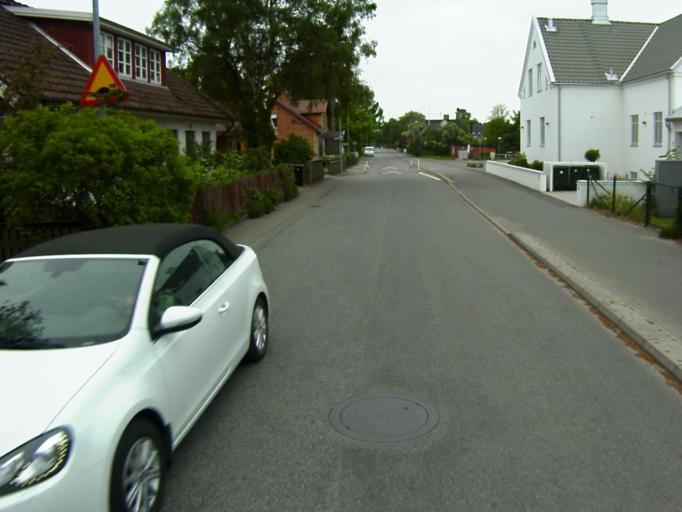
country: SE
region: Skane
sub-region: Kristianstads Kommun
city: Ahus
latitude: 55.9201
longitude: 14.2950
